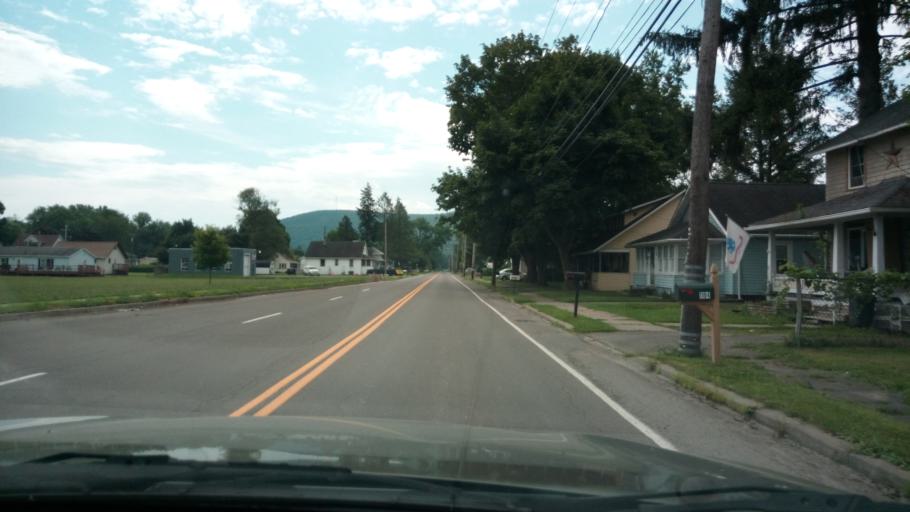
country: US
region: New York
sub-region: Chemung County
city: Southport
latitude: 42.0644
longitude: -76.7957
